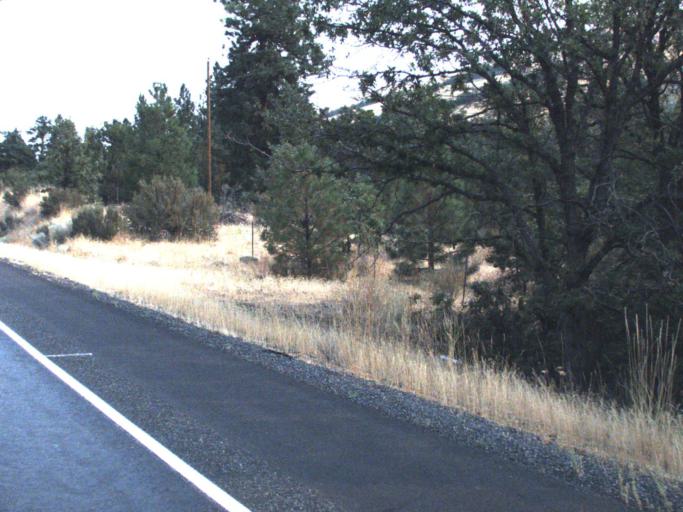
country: US
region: Washington
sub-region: Klickitat County
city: Goldendale
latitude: 46.0579
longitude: -120.5661
